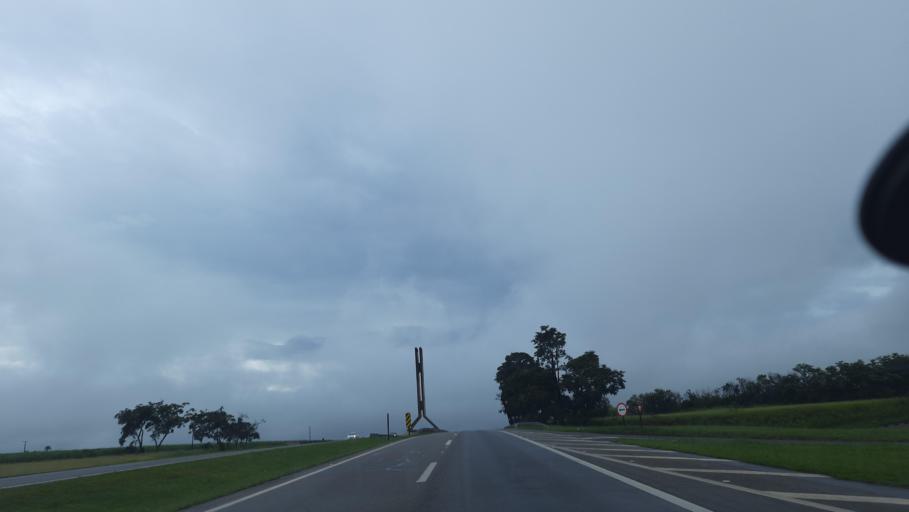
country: BR
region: Sao Paulo
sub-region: Aguai
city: Aguai
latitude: -22.1445
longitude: -46.9964
